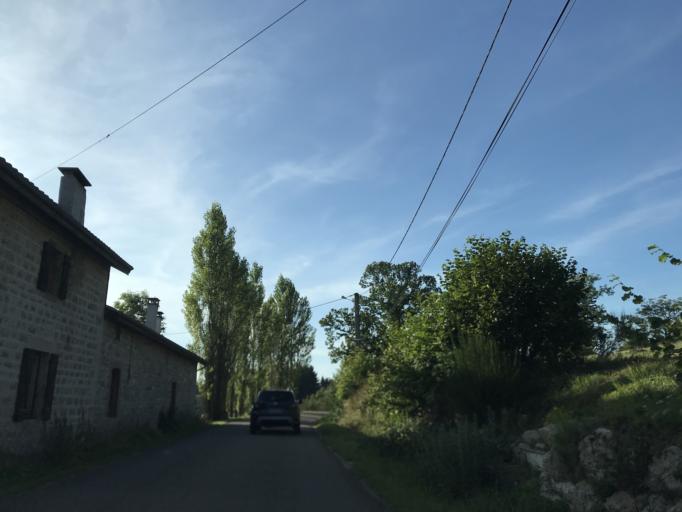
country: FR
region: Auvergne
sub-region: Departement du Puy-de-Dome
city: Job
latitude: 45.6955
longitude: 3.7299
